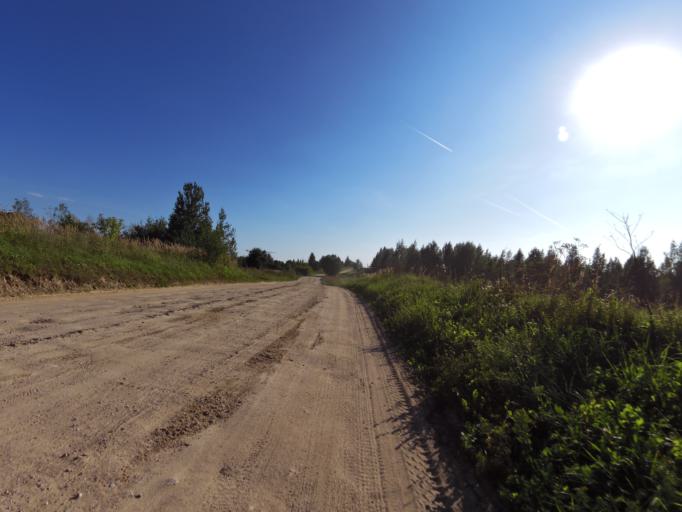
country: LT
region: Vilnius County
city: Pilaite
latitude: 54.7149
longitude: 25.1770
